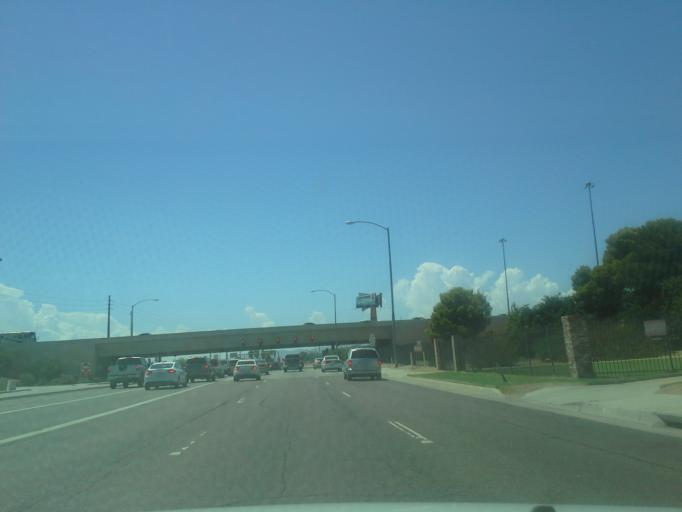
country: US
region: Arizona
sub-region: Maricopa County
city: Peoria
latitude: 33.5373
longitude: -112.2679
